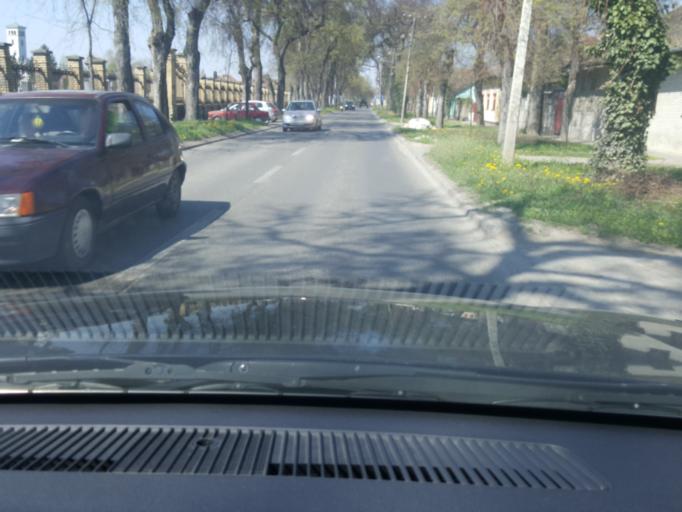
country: RS
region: Autonomna Pokrajina Vojvodina
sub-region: Zapadnobacki Okrug
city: Sombor
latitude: 45.7701
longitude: 19.1055
